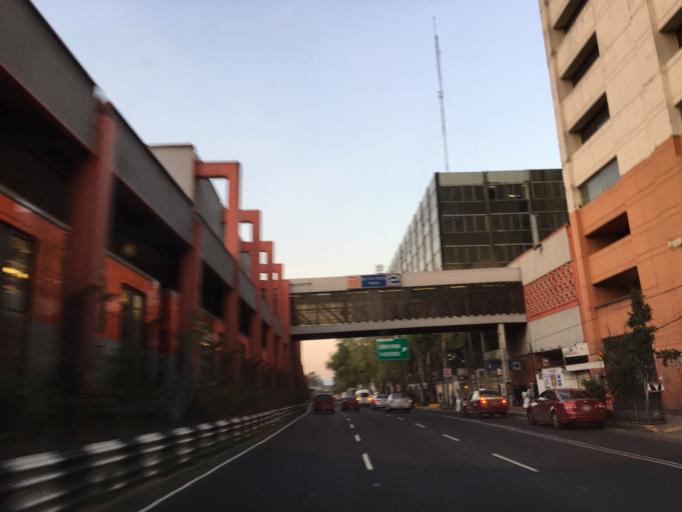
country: MX
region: Mexico City
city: Mexico City
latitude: 19.4156
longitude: -99.1345
